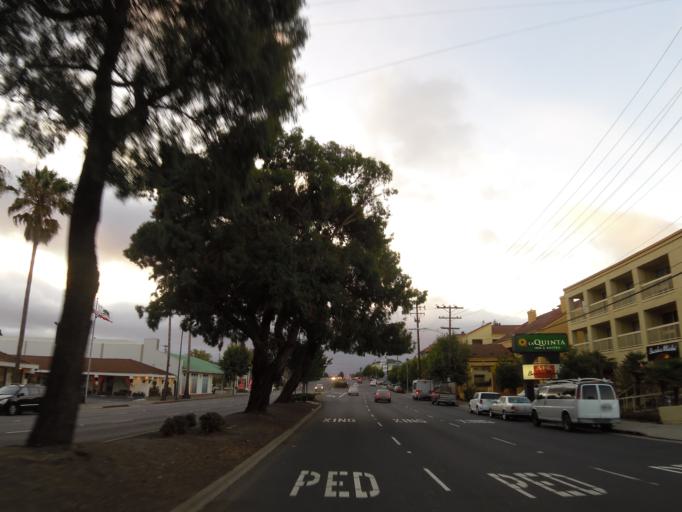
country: US
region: California
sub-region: San Mateo County
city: Millbrae
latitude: 37.6095
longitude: -122.4006
